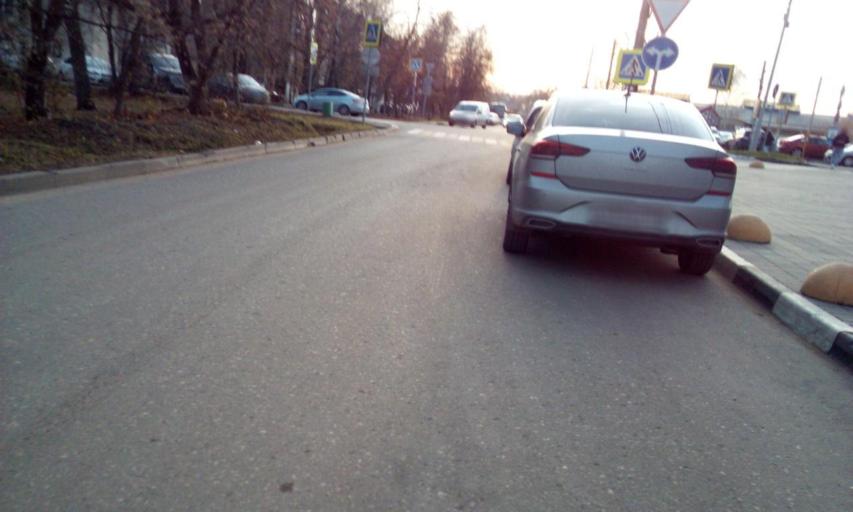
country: RU
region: Moskovskaya
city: Aprelevka
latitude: 55.5497
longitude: 37.0691
